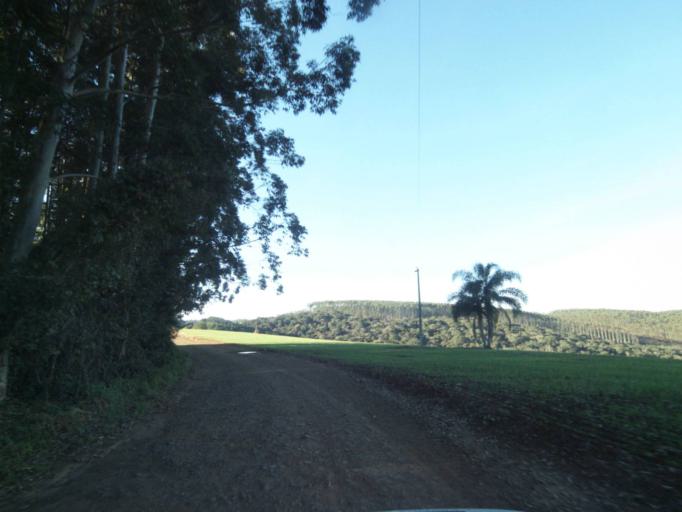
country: BR
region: Parana
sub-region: Telemaco Borba
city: Telemaco Borba
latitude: -24.4777
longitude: -50.5878
